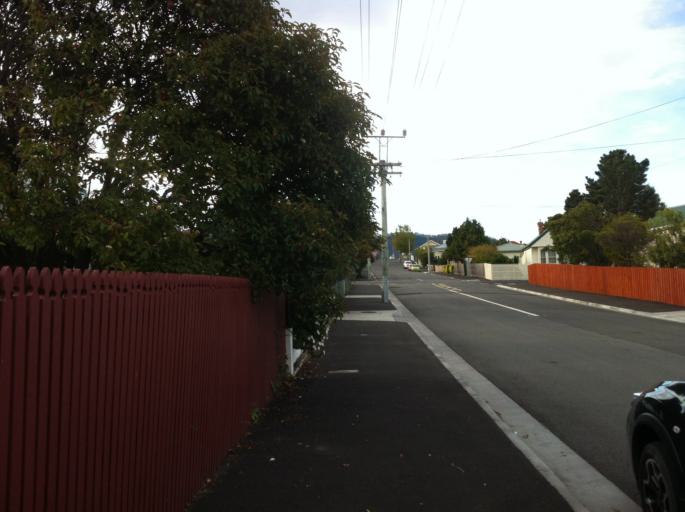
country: AU
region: Tasmania
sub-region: Glenorchy
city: Moonah
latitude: -42.8463
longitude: 147.3044
